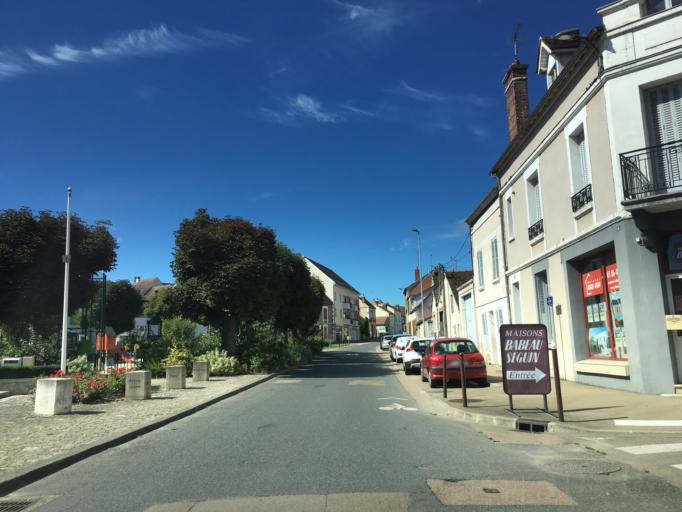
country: FR
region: Bourgogne
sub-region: Departement de l'Yonne
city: Auxerre
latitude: 47.7904
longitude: 3.5655
